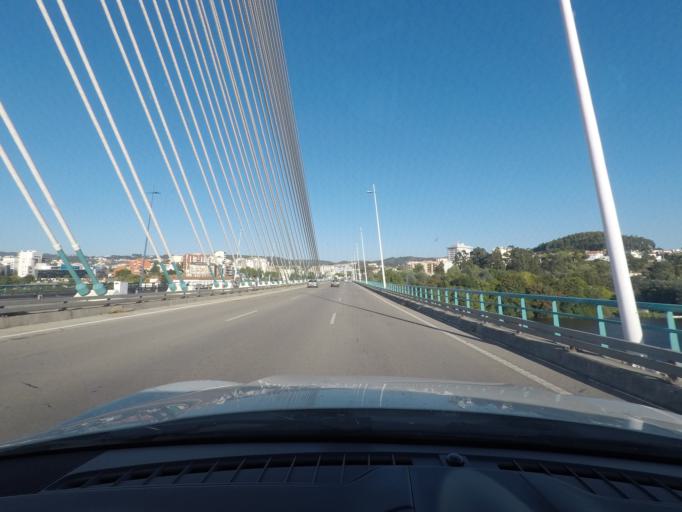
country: PT
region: Coimbra
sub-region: Coimbra
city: Coimbra
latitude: 40.1927
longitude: -8.4248
